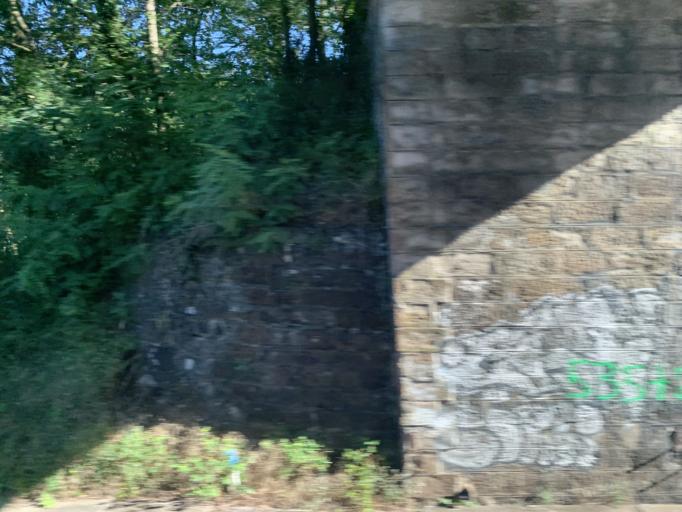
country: FR
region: Rhone-Alpes
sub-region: Departement du Rhone
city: Chassagny
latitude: 45.5779
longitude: 4.7344
